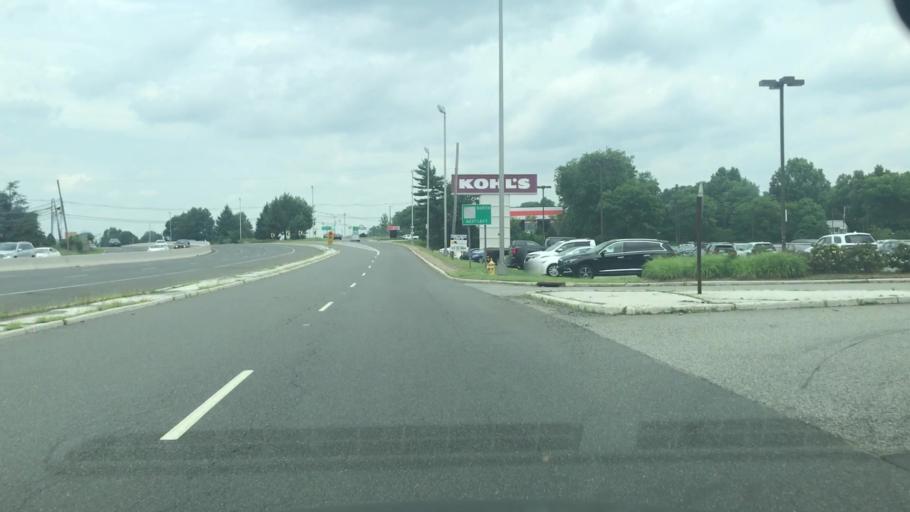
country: US
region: New Jersey
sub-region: Passaic County
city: Wayne
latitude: 40.9446
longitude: -74.2723
